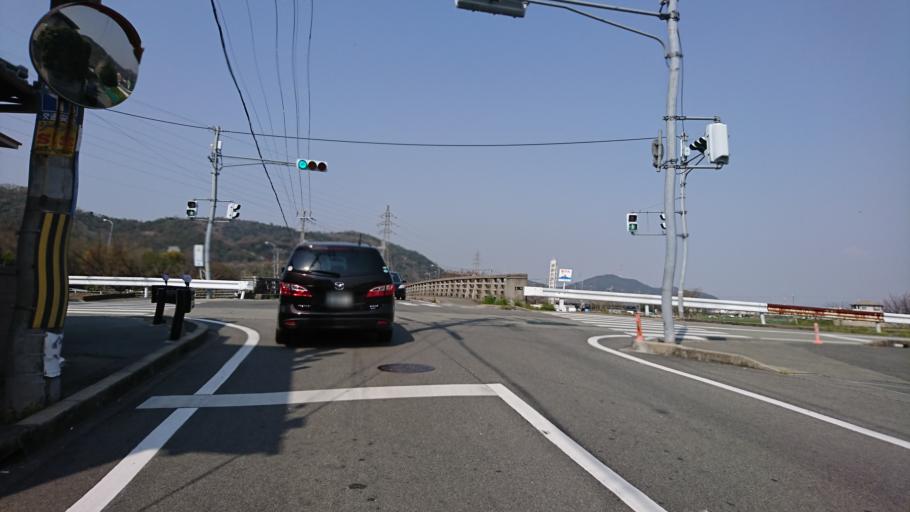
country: JP
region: Hyogo
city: Shirahamacho-usazakiminami
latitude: 34.7934
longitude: 134.7674
